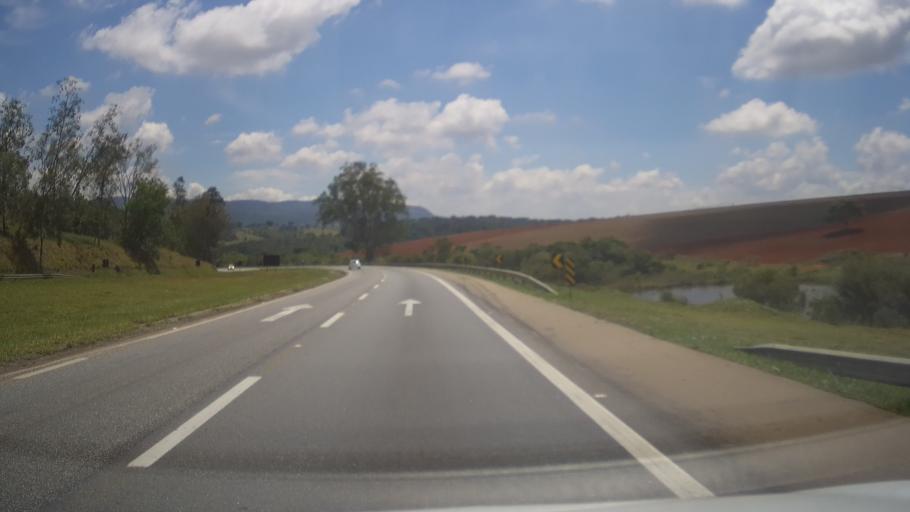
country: BR
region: Minas Gerais
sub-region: Sao Goncalo Do Sapucai
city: Sao Goncalo do Sapucai
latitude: -21.9297
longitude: -45.6114
